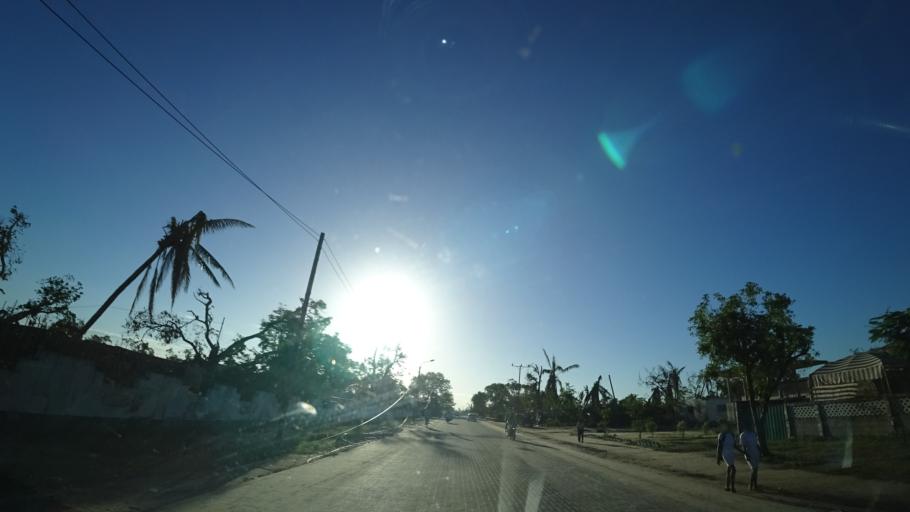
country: MZ
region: Sofala
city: Beira
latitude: -19.7468
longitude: 34.8487
